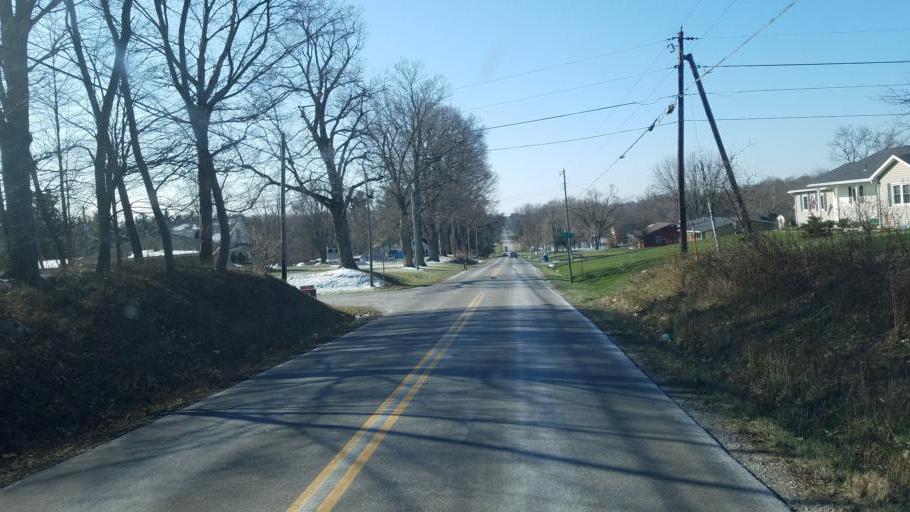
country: US
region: Ohio
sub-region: Knox County
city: Mount Vernon
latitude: 40.4272
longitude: -82.4877
